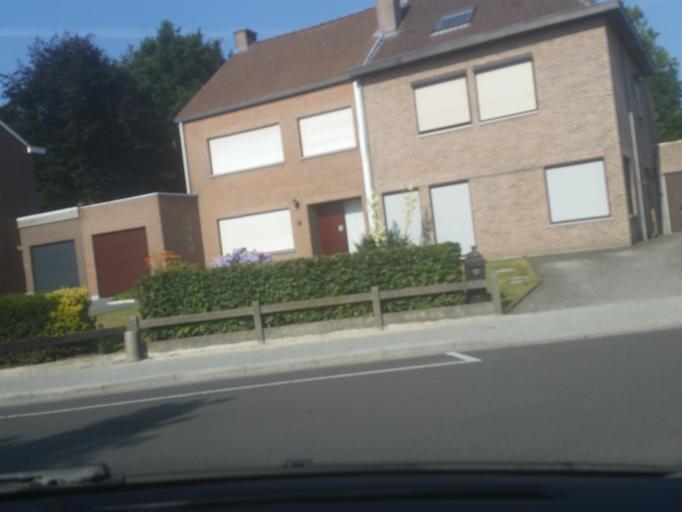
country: BE
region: Flanders
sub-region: Provincie Antwerpen
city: Mechelen
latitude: 51.0070
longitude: 4.4685
